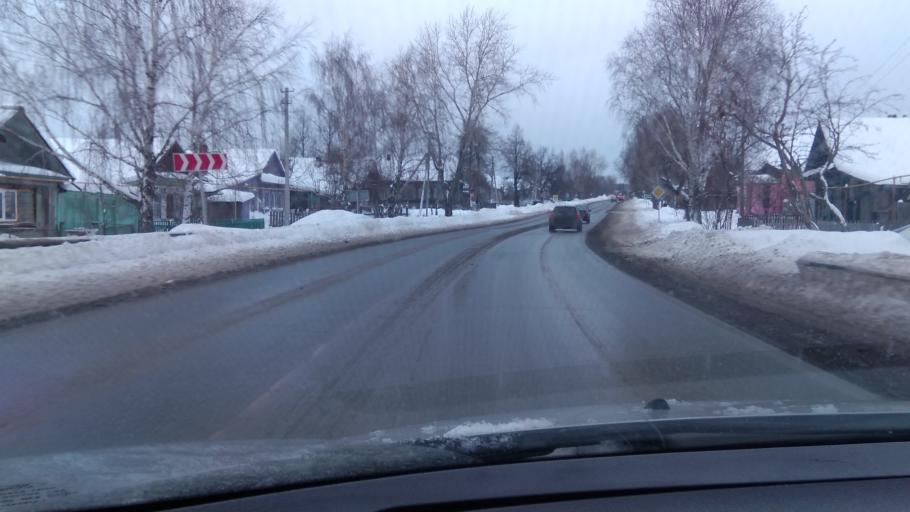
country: RU
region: Sverdlovsk
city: Nikolo-Pavlovskoye
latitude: 57.7865
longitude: 60.0553
